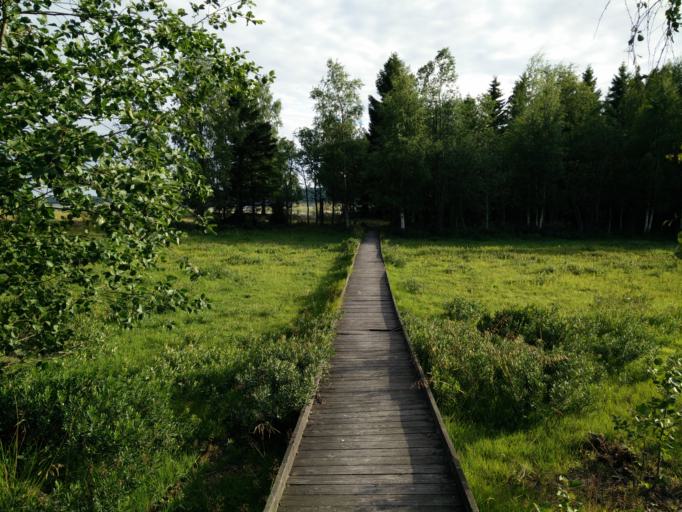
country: SE
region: Vaesternorrland
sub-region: Timra Kommun
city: Soraker
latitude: 62.4501
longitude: 17.4974
